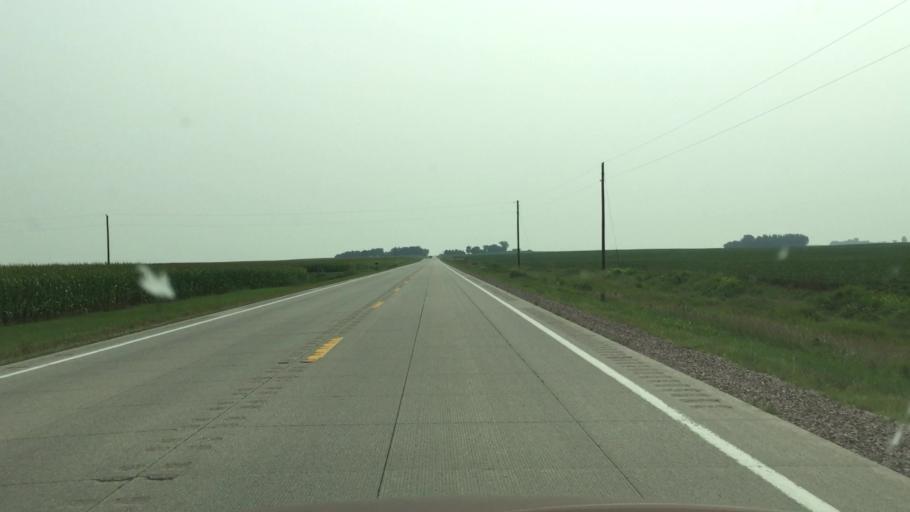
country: US
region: Iowa
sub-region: Osceola County
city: Sibley
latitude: 43.4327
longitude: -95.6807
